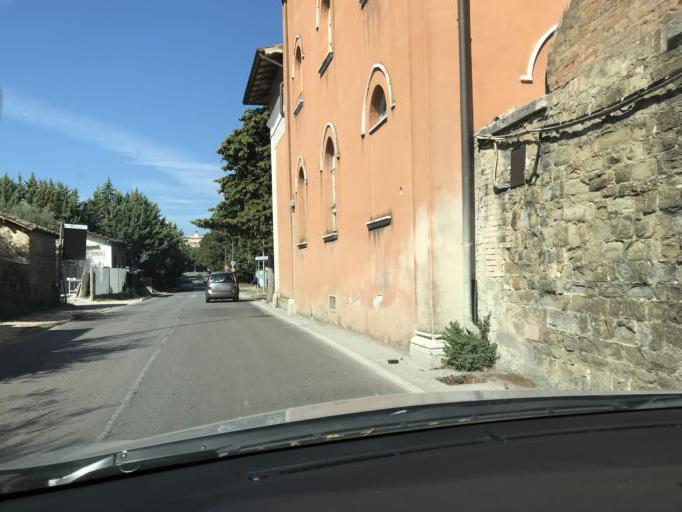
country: IT
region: Umbria
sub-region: Provincia di Perugia
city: Perugia
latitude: 43.1107
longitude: 12.4118
